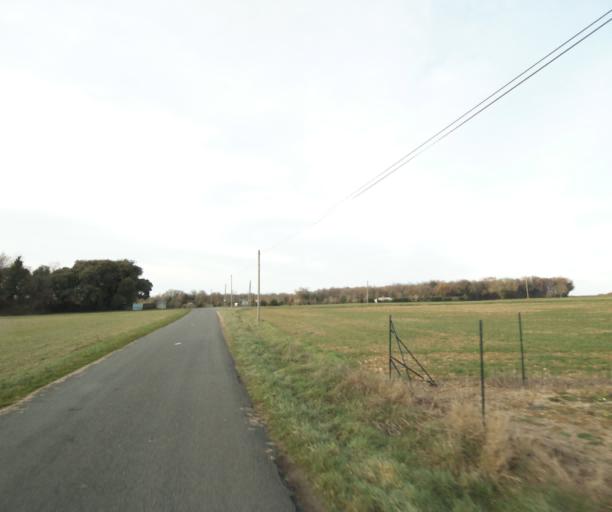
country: FR
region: Poitou-Charentes
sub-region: Departement de la Charente-Maritime
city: Saint-Hilaire-de-Villefranche
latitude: 45.8208
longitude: -0.5611
